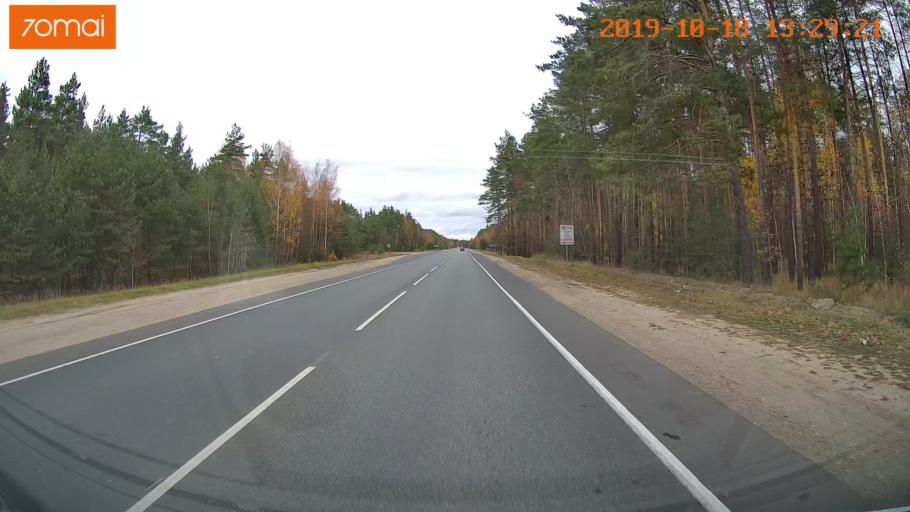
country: RU
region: Rjazan
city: Solotcha
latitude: 54.7933
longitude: 39.8743
